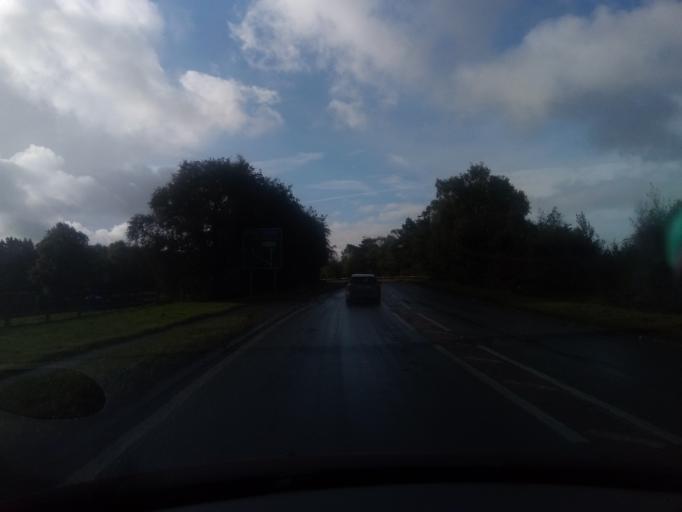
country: GB
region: England
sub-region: Cumbria
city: Carlisle
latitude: 54.9331
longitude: -2.9458
